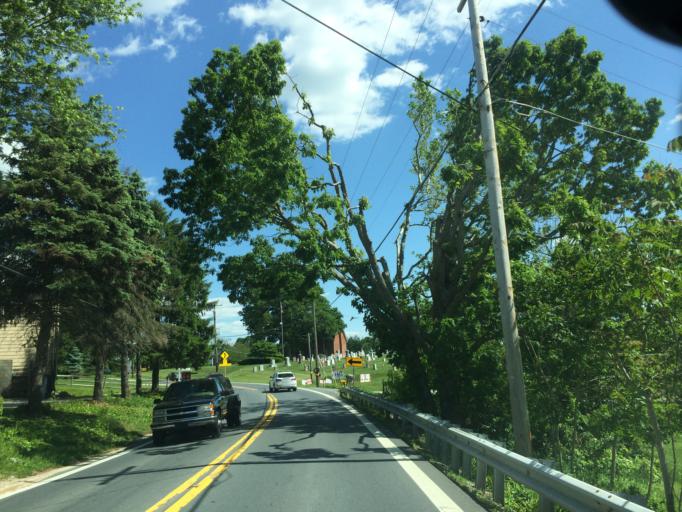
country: US
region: Maryland
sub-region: Carroll County
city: Westminster
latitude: 39.5143
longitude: -76.9764
